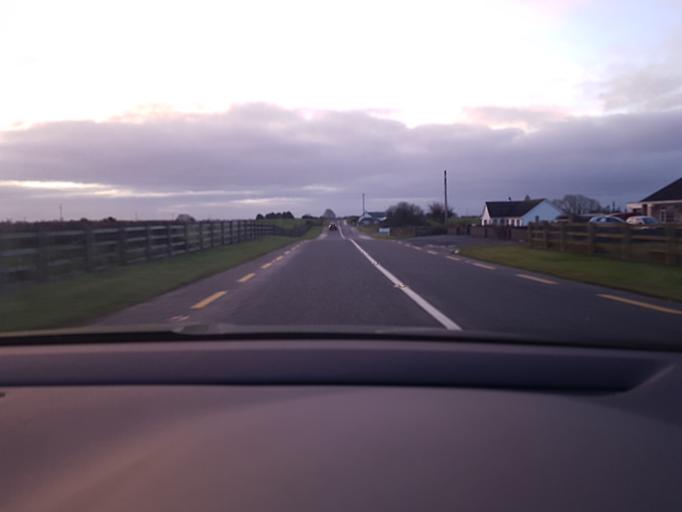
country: IE
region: Connaught
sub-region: County Galway
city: Tuam
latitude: 53.5443
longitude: -8.8924
